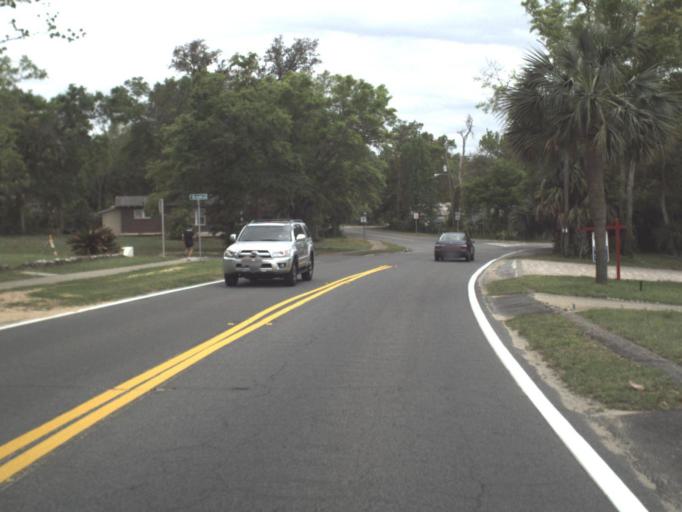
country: US
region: Florida
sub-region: Escambia County
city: East Pensacola Heights
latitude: 30.4327
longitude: -87.1825
